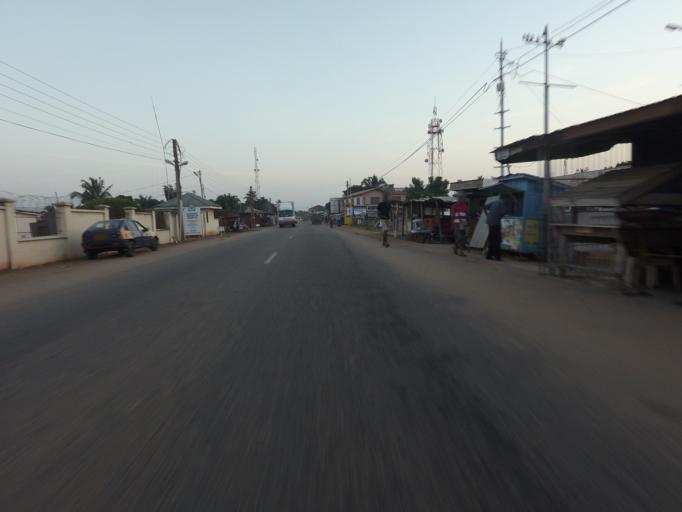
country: GH
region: Volta
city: Keta
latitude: 5.8913
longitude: 0.9848
